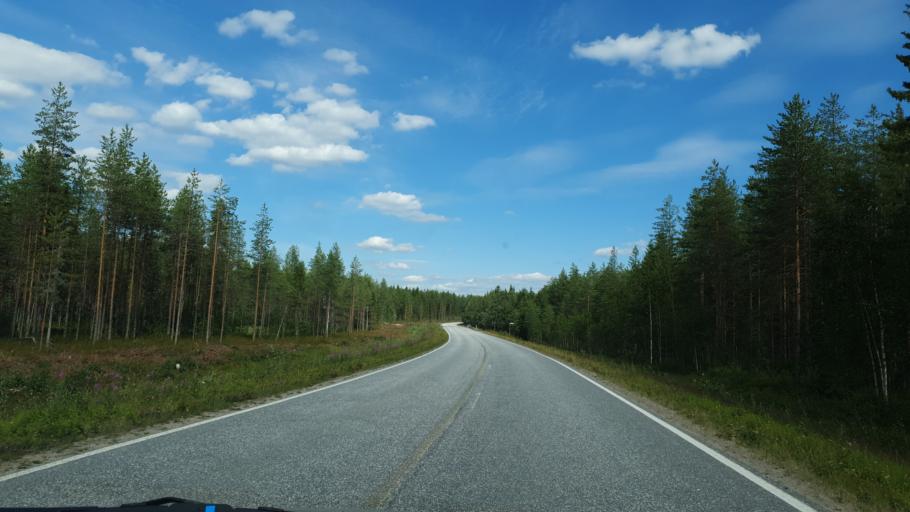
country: FI
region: Kainuu
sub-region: Kajaani
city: Sotkamo
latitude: 64.1622
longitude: 28.7535
